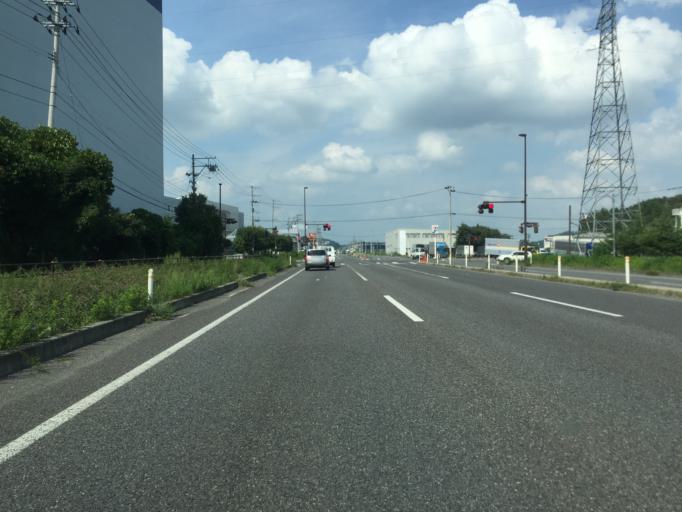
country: JP
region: Fukushima
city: Motomiya
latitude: 37.5273
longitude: 140.3960
